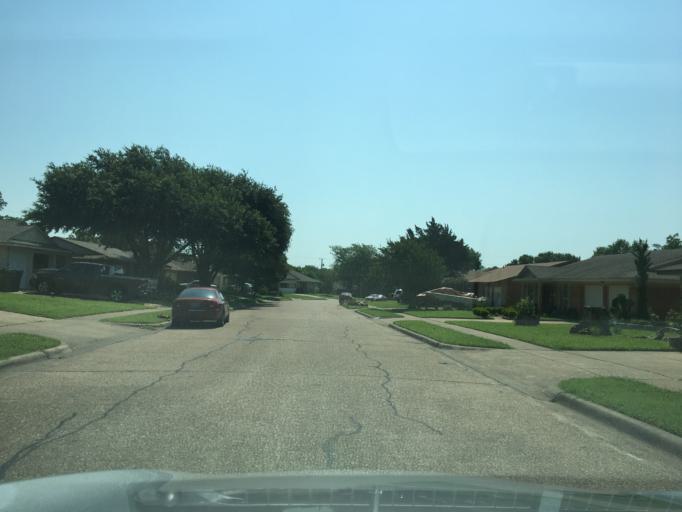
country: US
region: Texas
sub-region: Dallas County
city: Richardson
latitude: 32.9219
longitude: -96.6977
